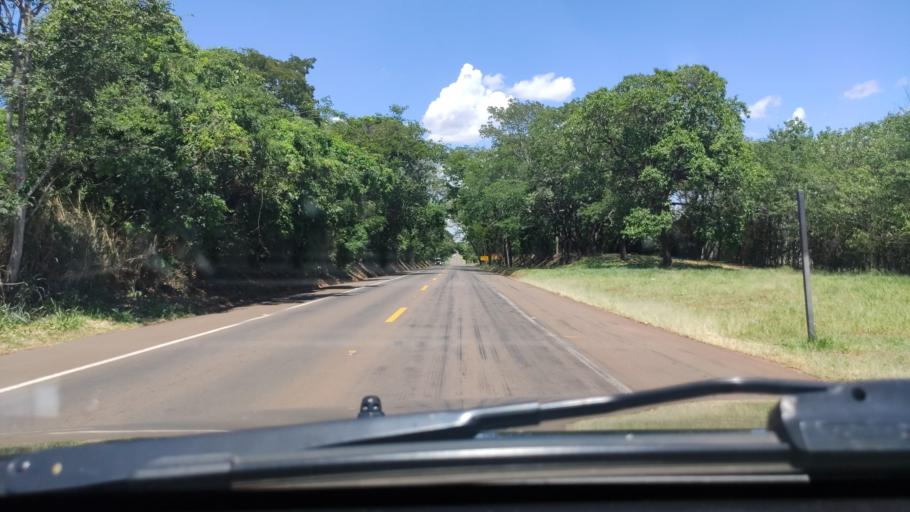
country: BR
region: Sao Paulo
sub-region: Boa Esperanca Do Sul
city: Boa Esperanca do Sul
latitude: -22.0691
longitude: -48.3765
